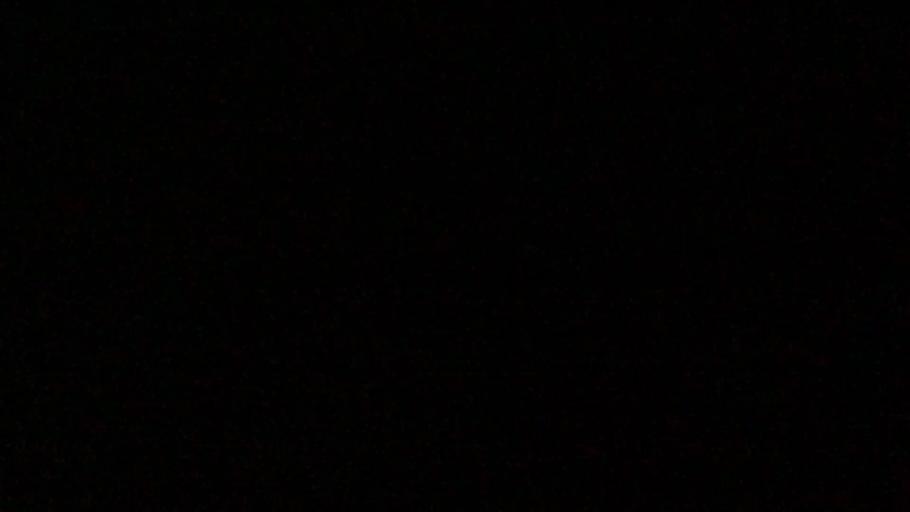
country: JP
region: Aomori
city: Kuroishi
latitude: 40.5184
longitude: 140.6042
